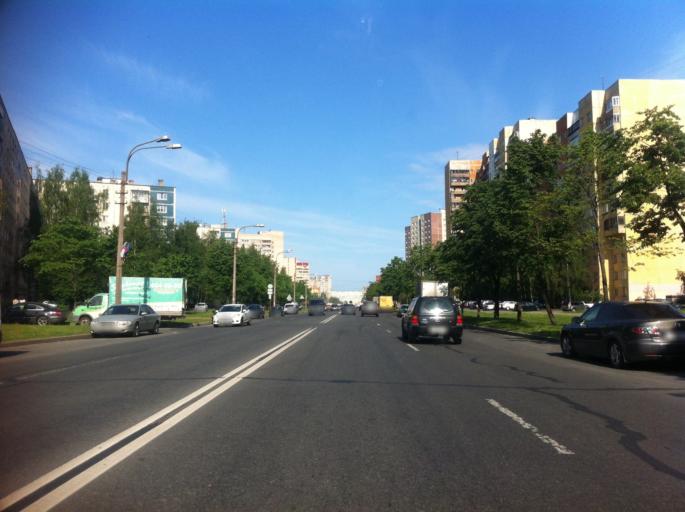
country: RU
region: St.-Petersburg
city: Uritsk
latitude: 59.8507
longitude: 30.2065
